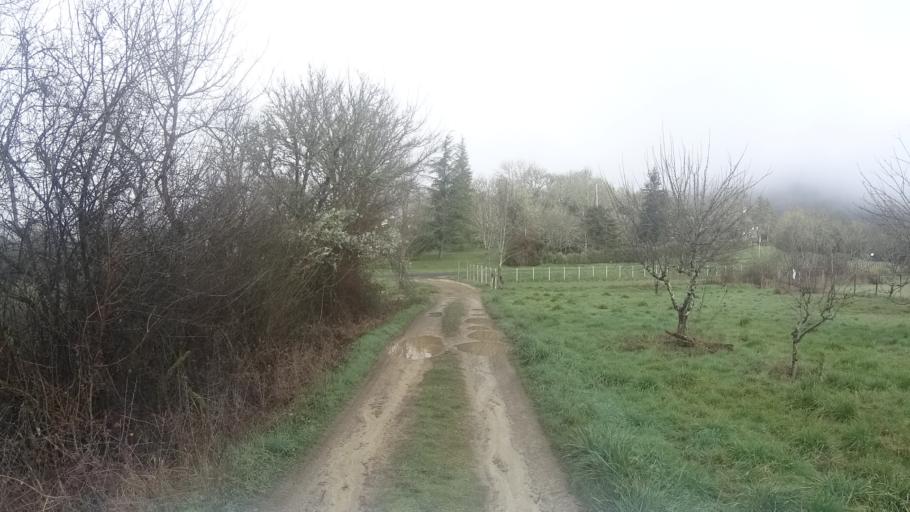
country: FR
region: Aquitaine
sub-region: Departement de la Dordogne
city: Terrasson-Lavilledieu
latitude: 45.1023
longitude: 1.2663
